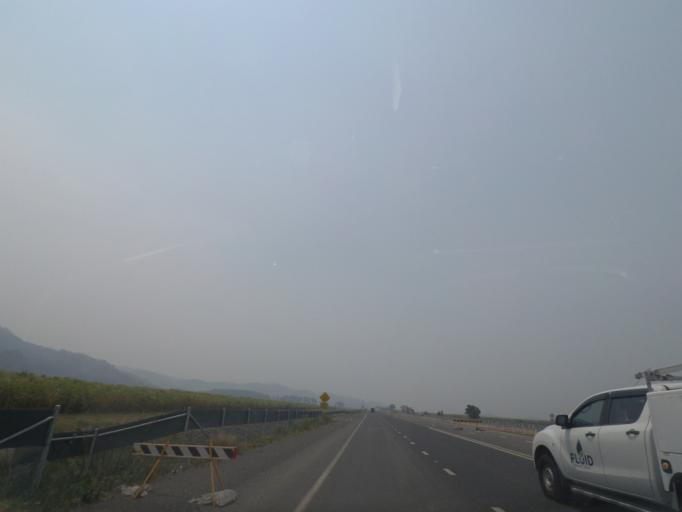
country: AU
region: New South Wales
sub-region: Ballina
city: Ballina
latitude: -28.9006
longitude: 153.4800
